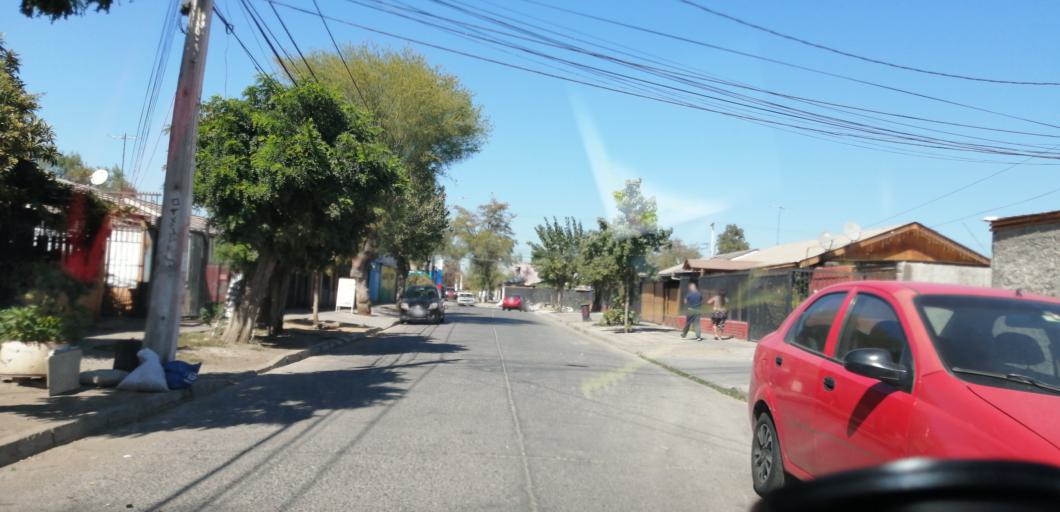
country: CL
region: Santiago Metropolitan
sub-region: Provincia de Santiago
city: Lo Prado
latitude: -33.4342
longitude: -70.7602
